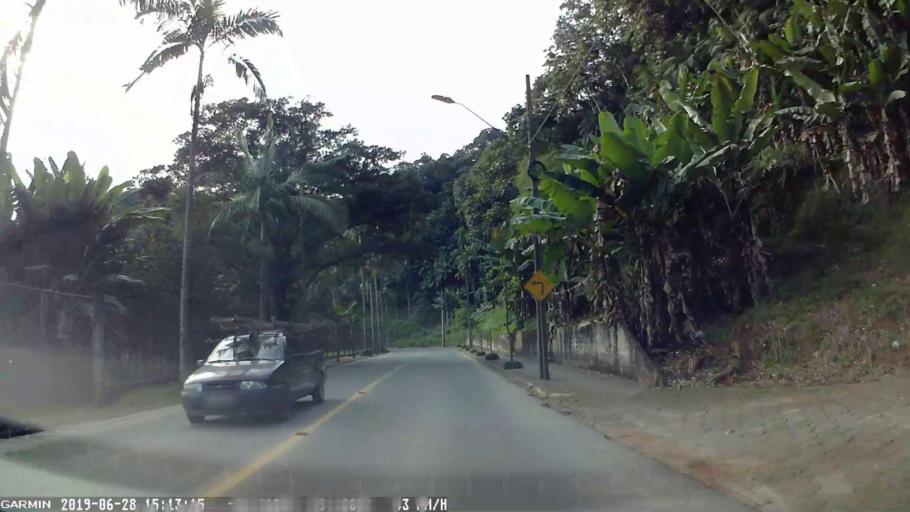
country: BR
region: Santa Catarina
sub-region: Jaragua Do Sul
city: Jaragua do Sul
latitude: -26.5103
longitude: -49.1270
